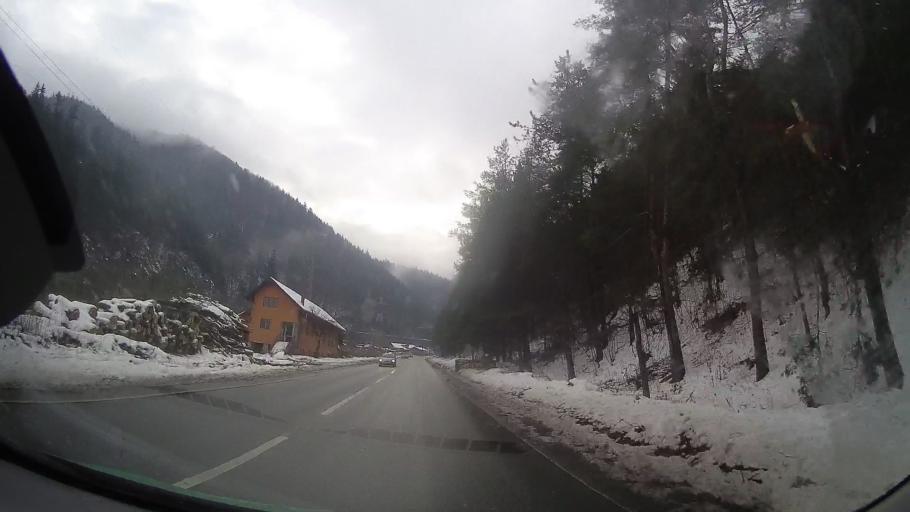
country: RO
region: Neamt
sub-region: Comuna Bicaz
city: Bicaz
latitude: 46.8980
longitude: 26.0545
